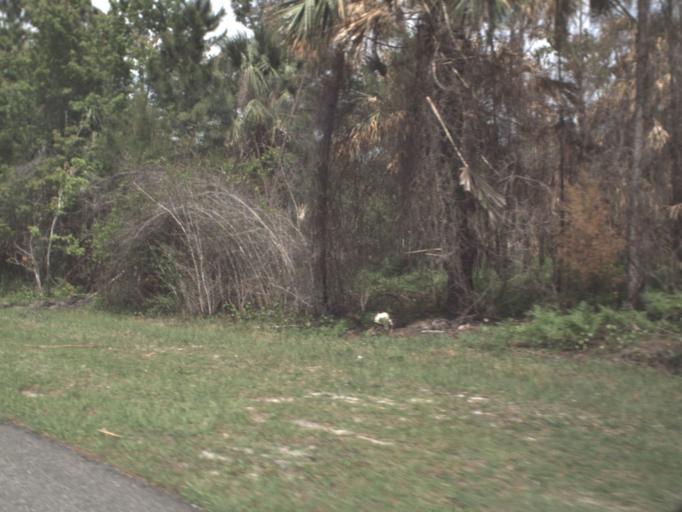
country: US
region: Florida
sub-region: Flagler County
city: Bunnell
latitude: 29.3819
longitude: -81.3100
